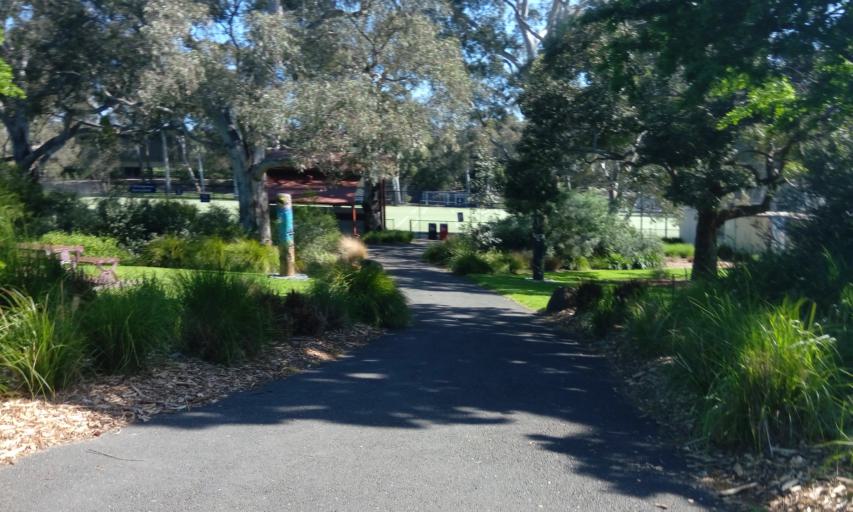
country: AU
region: Victoria
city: Toorak
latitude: -37.8356
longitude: 145.0283
